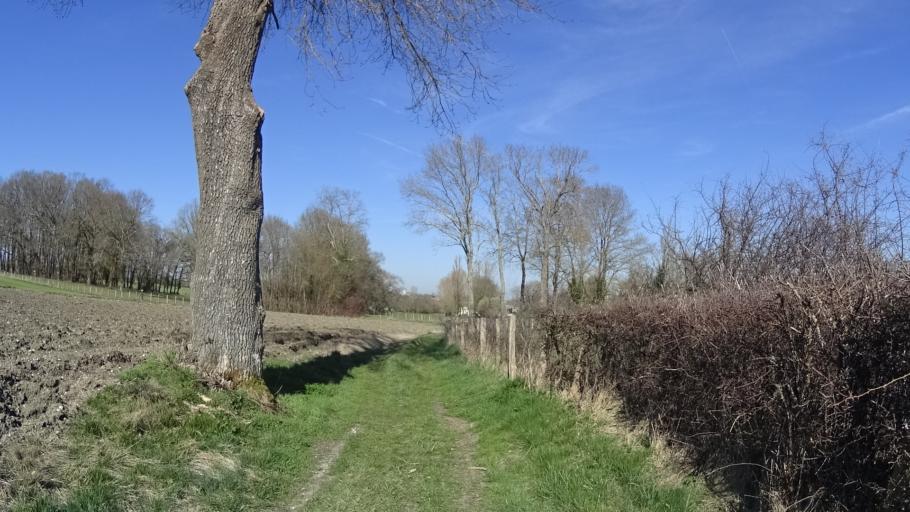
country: FR
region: Aquitaine
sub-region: Departement de la Dordogne
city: Riberac
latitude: 45.2266
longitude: 0.3334
